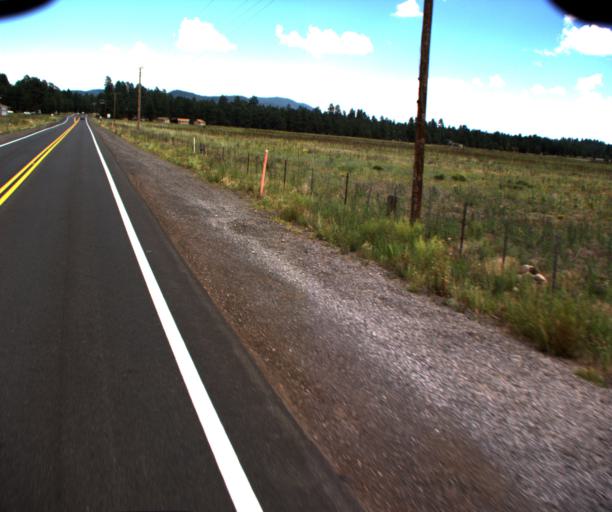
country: US
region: Arizona
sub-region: Coconino County
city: Flagstaff
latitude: 35.2683
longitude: -111.7240
